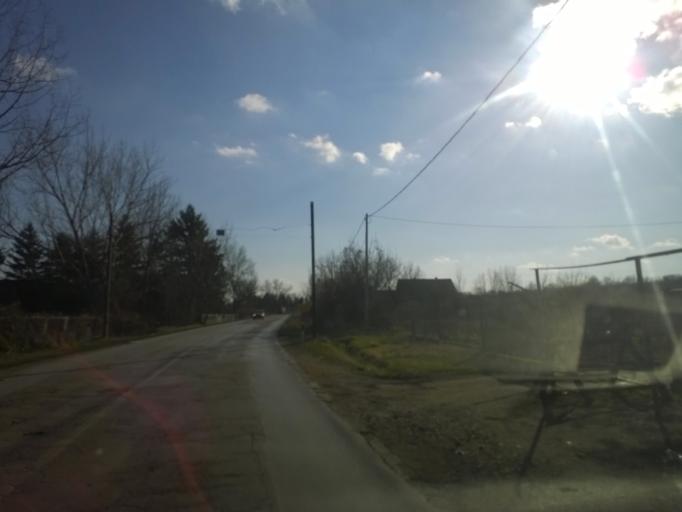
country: RS
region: Central Serbia
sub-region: Podunavski Okrug
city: Smederevo
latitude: 44.5871
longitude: 20.9745
